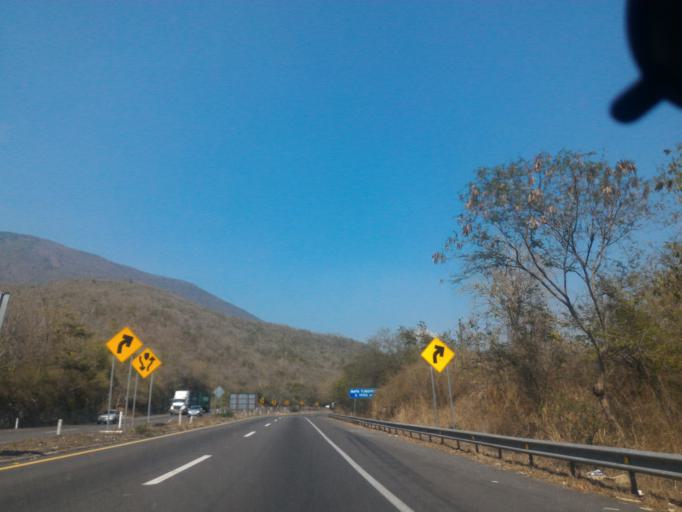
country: MX
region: Colima
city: Ixtlahuacan
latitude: 19.0297
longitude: -103.7946
